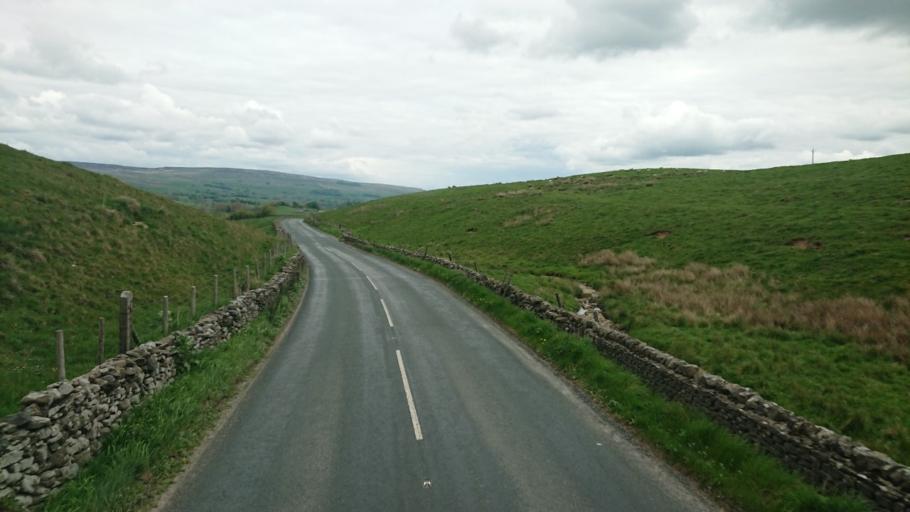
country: GB
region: England
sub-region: County Durham
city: Bowes
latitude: 54.3024
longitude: -2.1427
